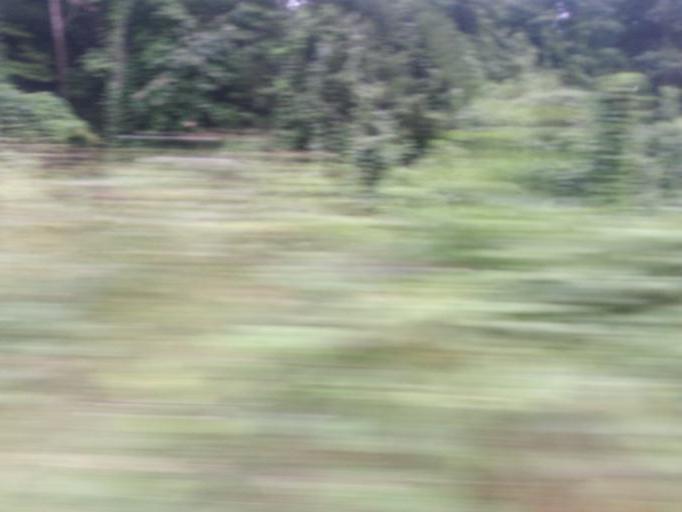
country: US
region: Tennessee
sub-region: Anderson County
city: Clinton
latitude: 36.1444
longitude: -84.2110
